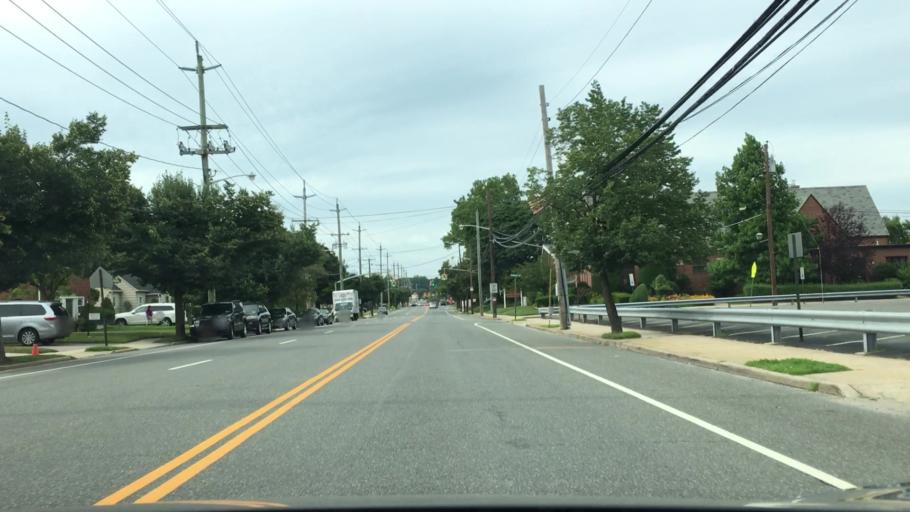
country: US
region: New York
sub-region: Nassau County
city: North New Hyde Park
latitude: 40.7510
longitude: -73.6864
